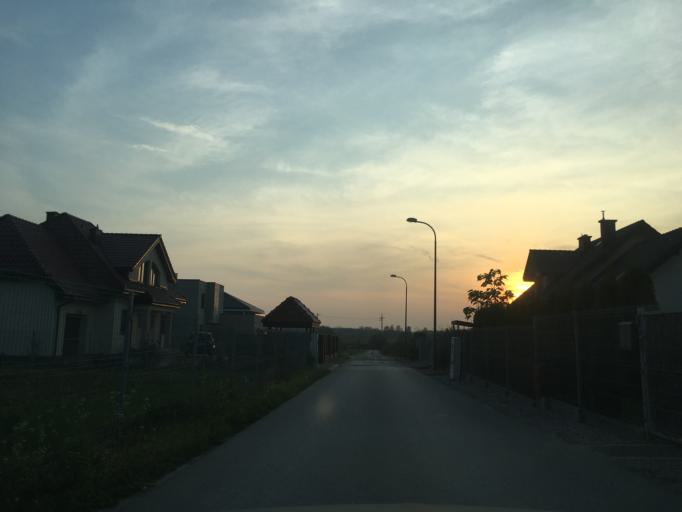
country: PL
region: Masovian Voivodeship
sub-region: Powiat piaseczynski
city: Lesznowola
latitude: 52.0527
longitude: 20.9263
